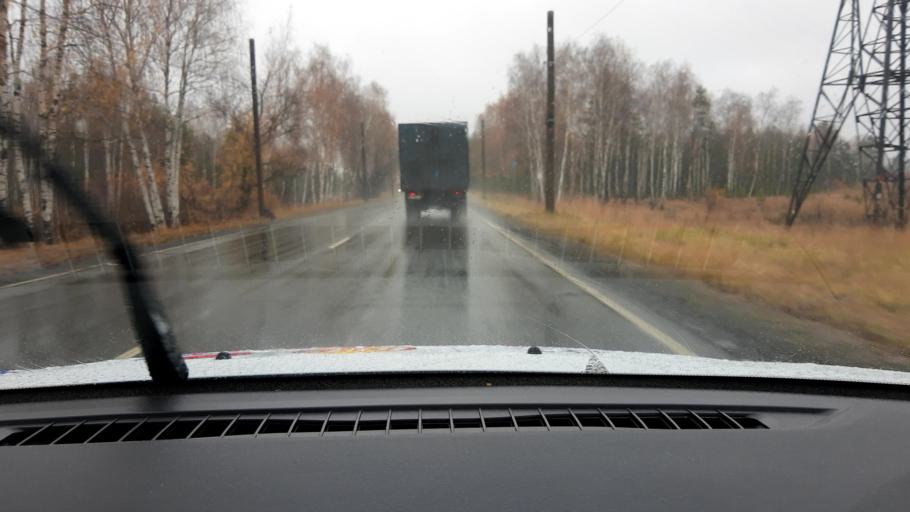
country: RU
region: Nizjnij Novgorod
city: Babino
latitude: 56.2871
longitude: 43.5880
